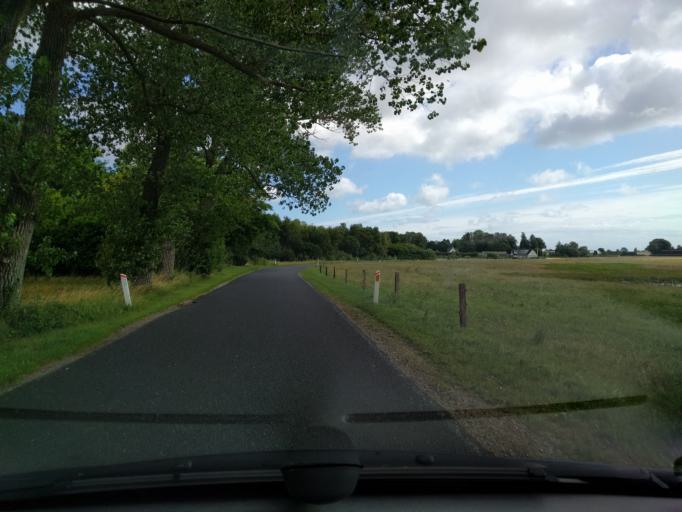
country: DK
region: South Denmark
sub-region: Kerteminde Kommune
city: Langeskov
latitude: 55.3886
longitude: 10.5922
